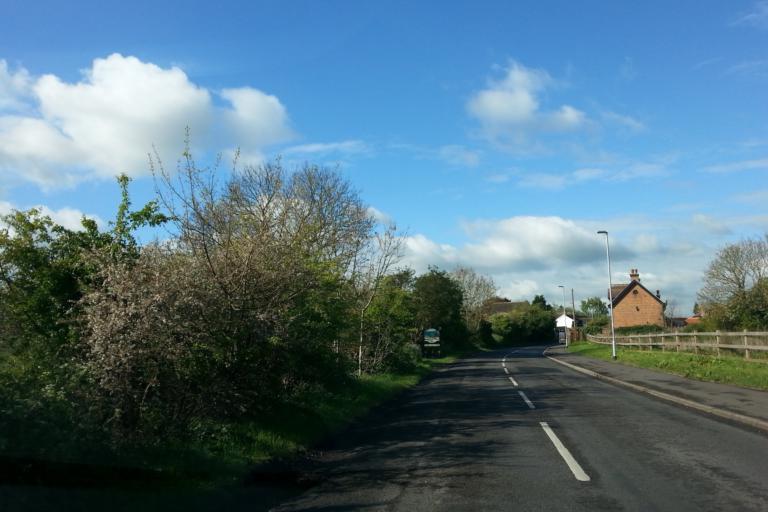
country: GB
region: England
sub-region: Nottinghamshire
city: Cotgrave
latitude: 52.9135
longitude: -1.0346
